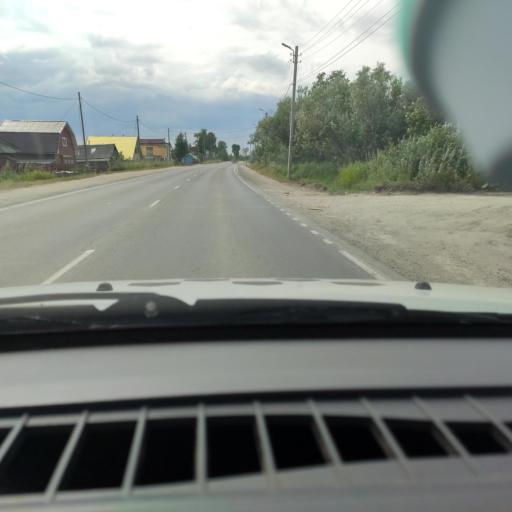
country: RU
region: Perm
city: Solikamsk
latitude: 59.6783
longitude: 56.7766
